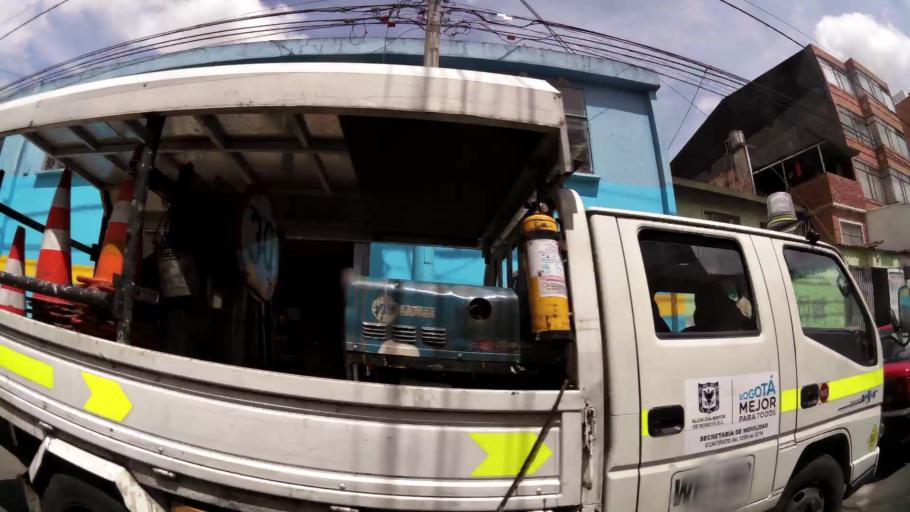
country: CO
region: Bogota D.C.
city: Barrio San Luis
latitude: 4.7016
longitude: -74.1092
